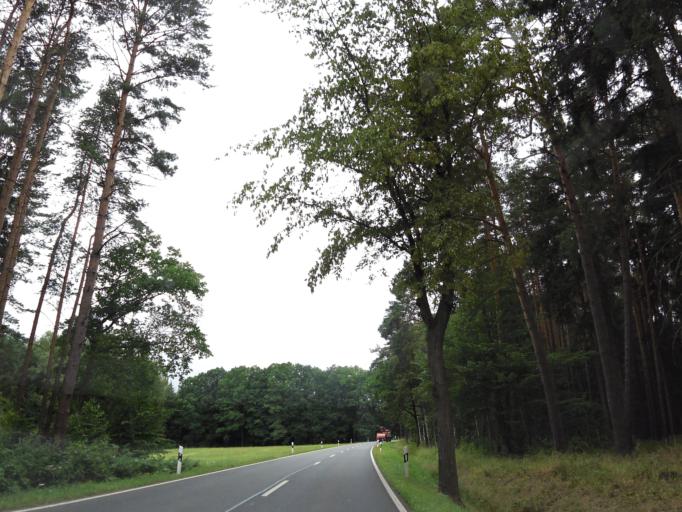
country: DE
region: Thuringia
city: Bad Klosterlausnitz
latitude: 50.9293
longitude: 11.8632
